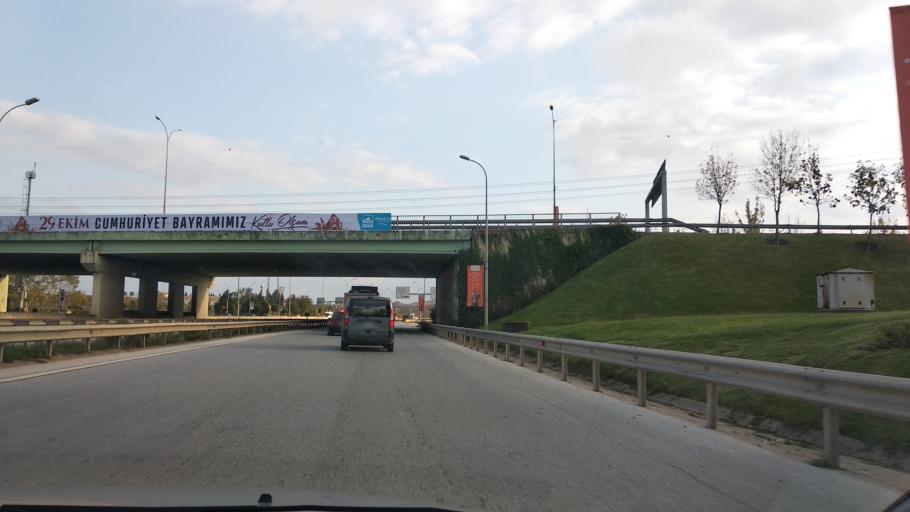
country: TR
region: Istanbul
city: Pendik
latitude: 40.9152
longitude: 29.3239
